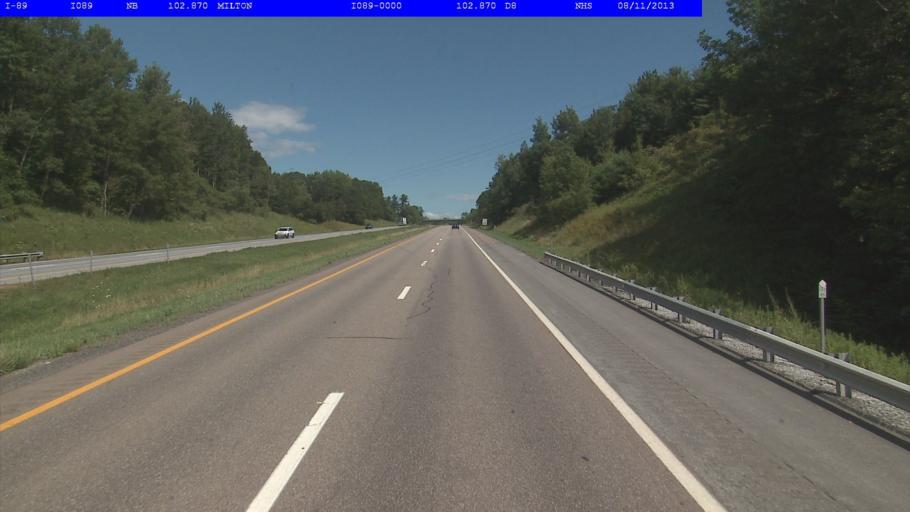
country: US
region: Vermont
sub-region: Chittenden County
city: Milton
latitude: 44.6548
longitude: -73.1391
